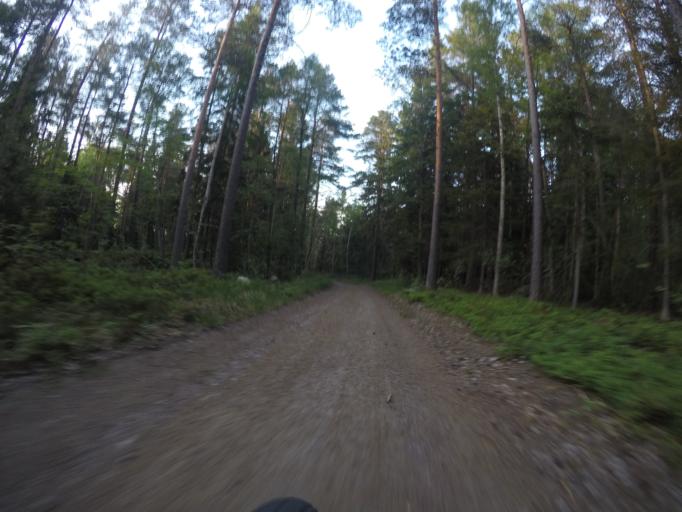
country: SE
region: Soedermanland
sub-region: Eskilstuna Kommun
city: Eskilstuna
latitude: 59.3449
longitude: 16.5114
